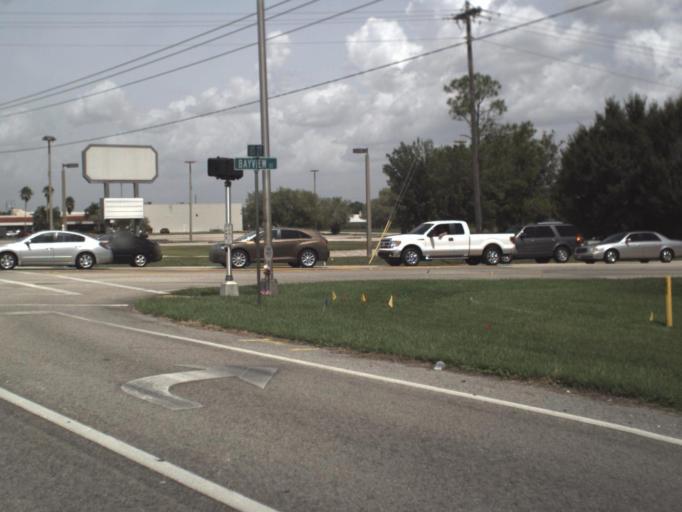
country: US
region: Florida
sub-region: Highlands County
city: Sebring
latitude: 27.5079
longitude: -81.4924
